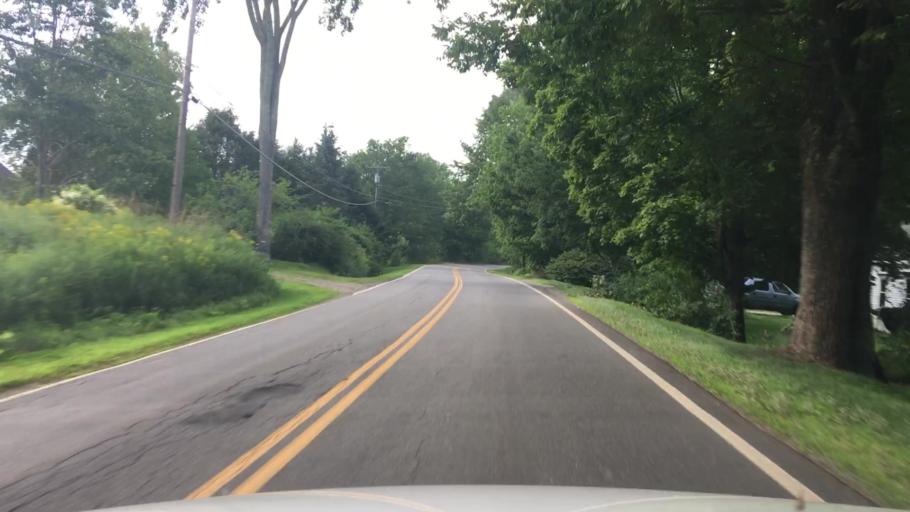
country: US
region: Maine
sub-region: Lincoln County
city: Waldoboro
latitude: 44.1415
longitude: -69.3720
